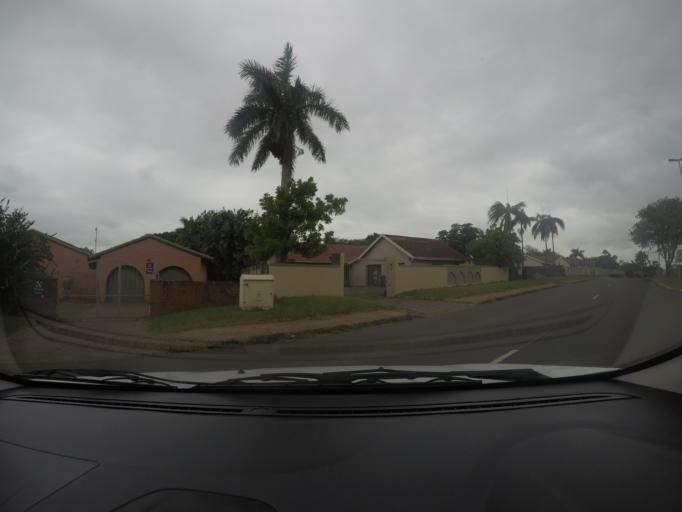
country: ZA
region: KwaZulu-Natal
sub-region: uThungulu District Municipality
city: Empangeni
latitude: -28.7643
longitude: 31.8958
